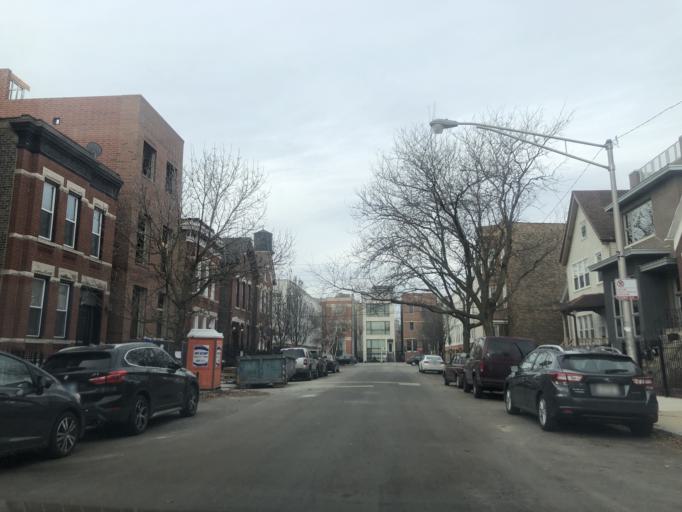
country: US
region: Illinois
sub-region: Cook County
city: Chicago
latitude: 41.9083
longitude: -87.6710
